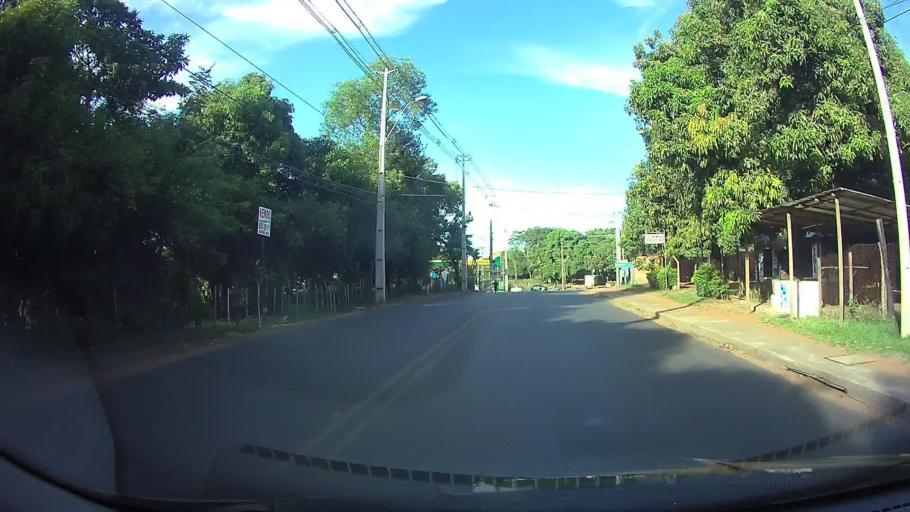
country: PY
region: Central
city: San Antonio
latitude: -25.4070
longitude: -57.5729
